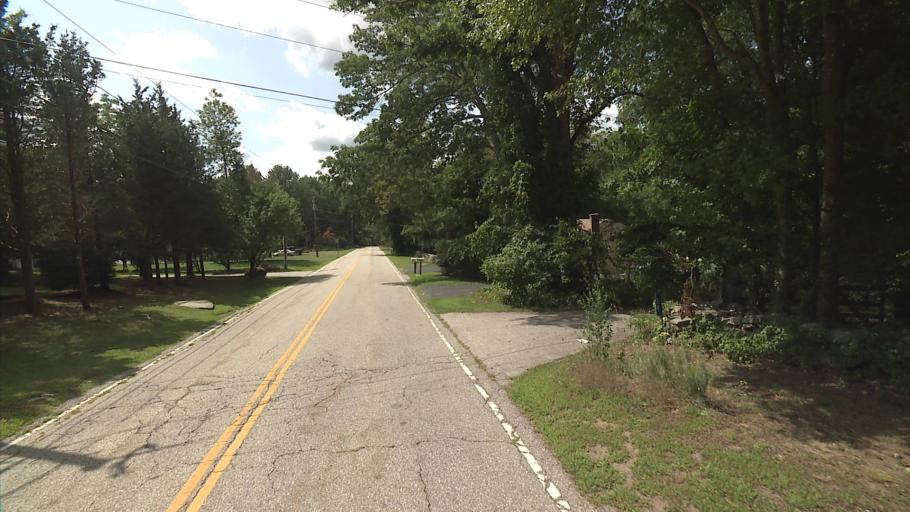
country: US
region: Connecticut
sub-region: New London County
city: Lisbon
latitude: 41.6171
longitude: -72.0248
